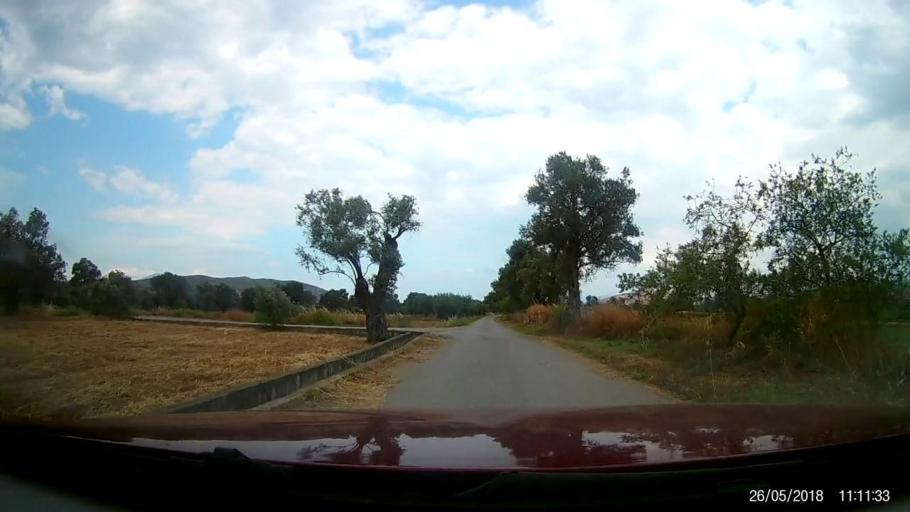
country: GR
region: Central Greece
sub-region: Nomos Evvoias
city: Mytikas
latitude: 38.4468
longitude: 23.6599
